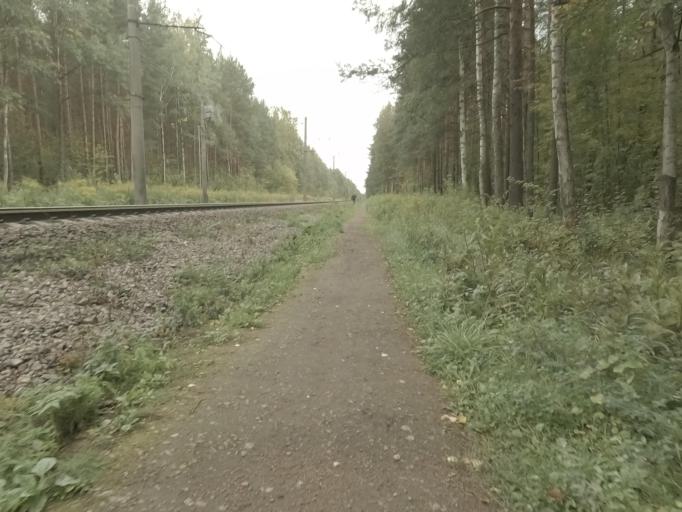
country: RU
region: St.-Petersburg
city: Krasnogvargeisky
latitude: 59.9668
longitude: 30.5121
